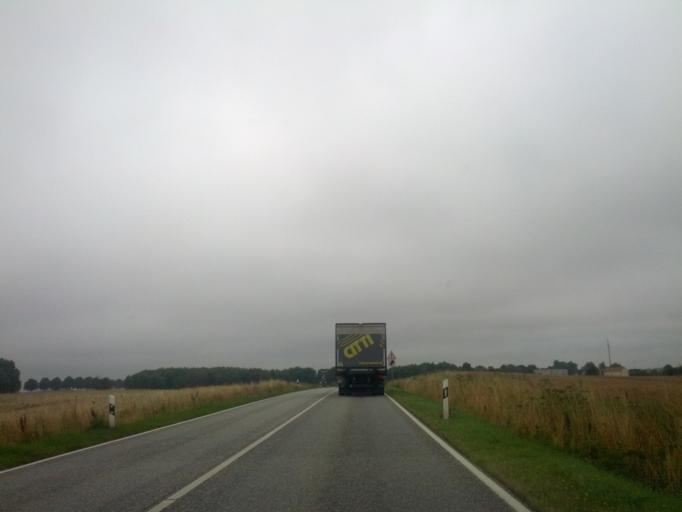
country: DE
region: Mecklenburg-Vorpommern
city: Sellin
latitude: 53.9668
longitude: 11.6186
